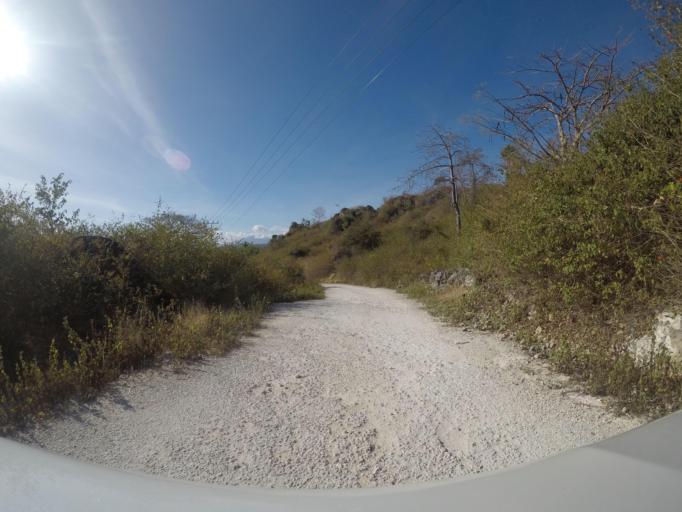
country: TL
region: Baucau
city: Baucau
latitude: -8.4494
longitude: 126.4278
